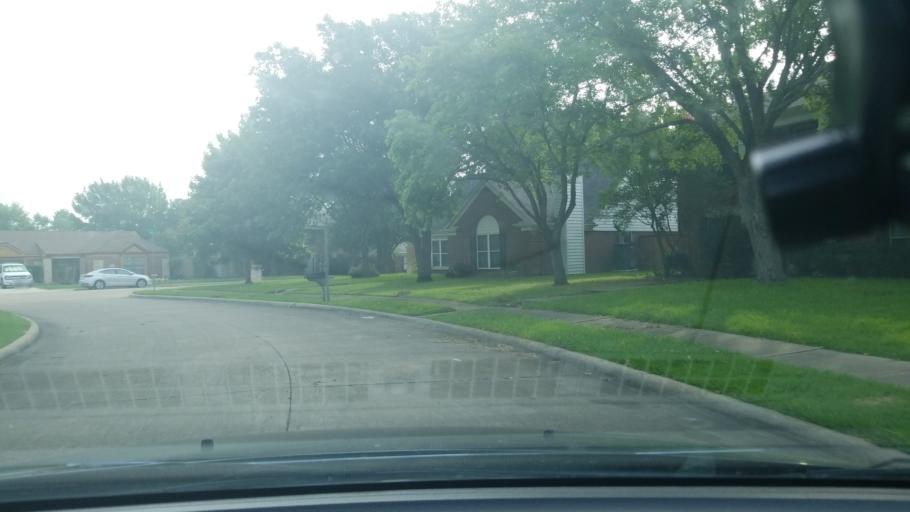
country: US
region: Texas
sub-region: Dallas County
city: Mesquite
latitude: 32.7880
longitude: -96.6494
